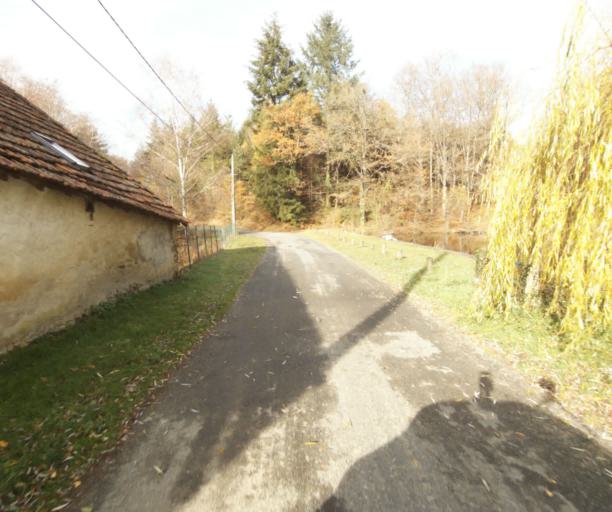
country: FR
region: Limousin
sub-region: Departement de la Correze
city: Sainte-Fortunade
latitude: 45.1968
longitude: 1.7355
